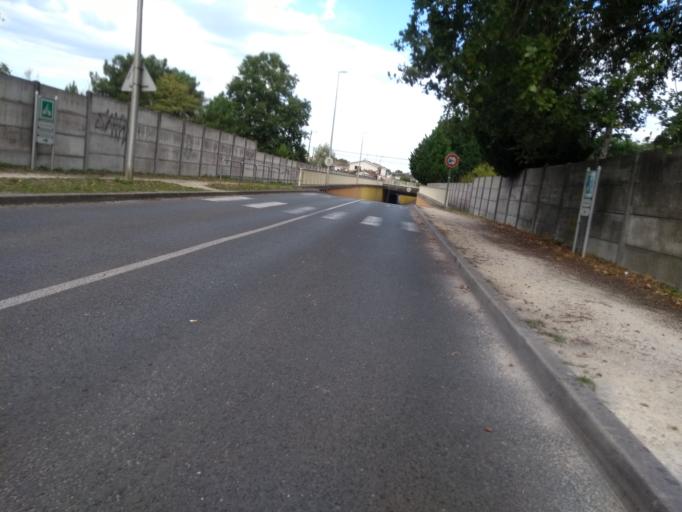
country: FR
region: Aquitaine
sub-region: Departement de la Gironde
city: Cestas
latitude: 44.7821
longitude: -0.6781
